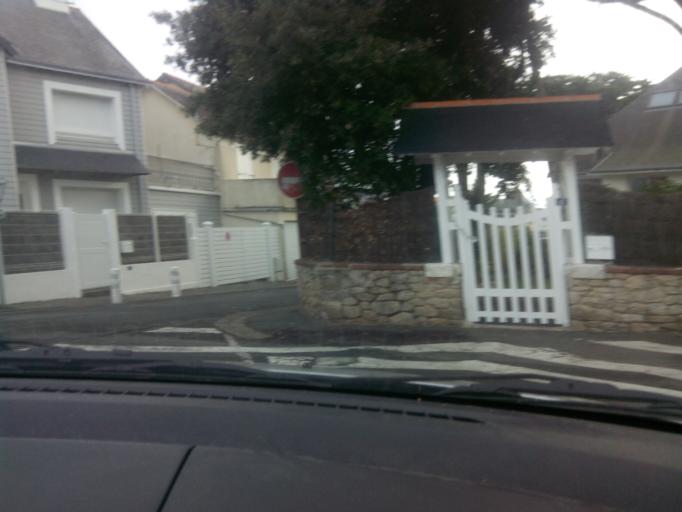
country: FR
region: Pays de la Loire
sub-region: Departement de la Loire-Atlantique
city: Pornichet
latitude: 47.2690
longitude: -2.3456
